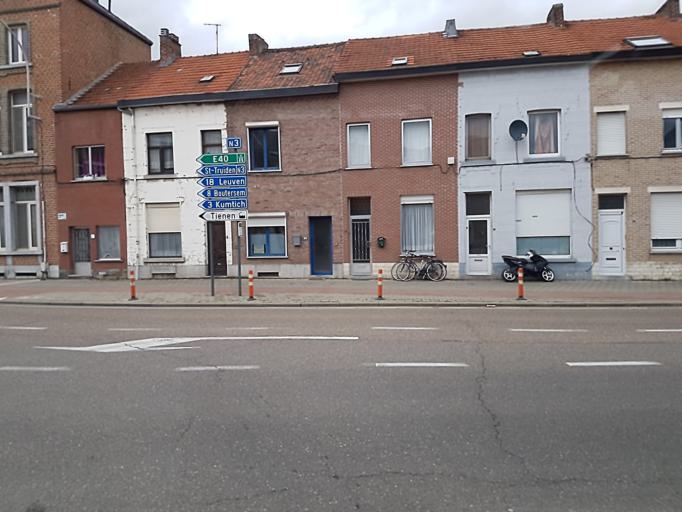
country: BE
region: Flanders
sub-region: Provincie Vlaams-Brabant
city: Tienen
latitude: 50.8113
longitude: 4.9252
